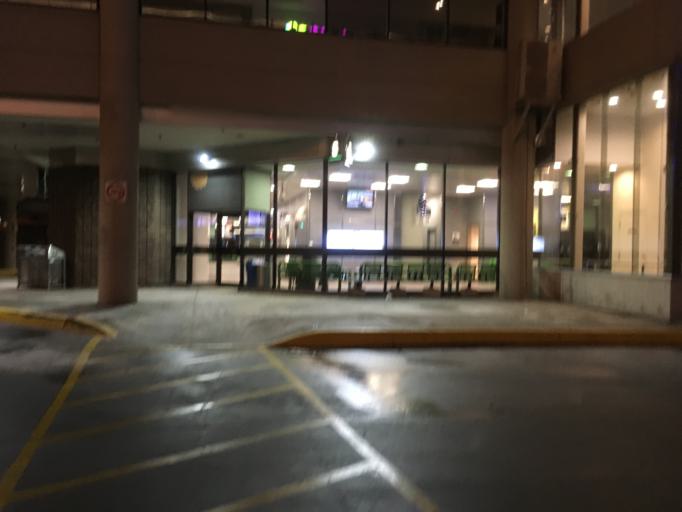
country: CA
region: Ontario
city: Toronto
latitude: 43.7254
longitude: -79.4491
